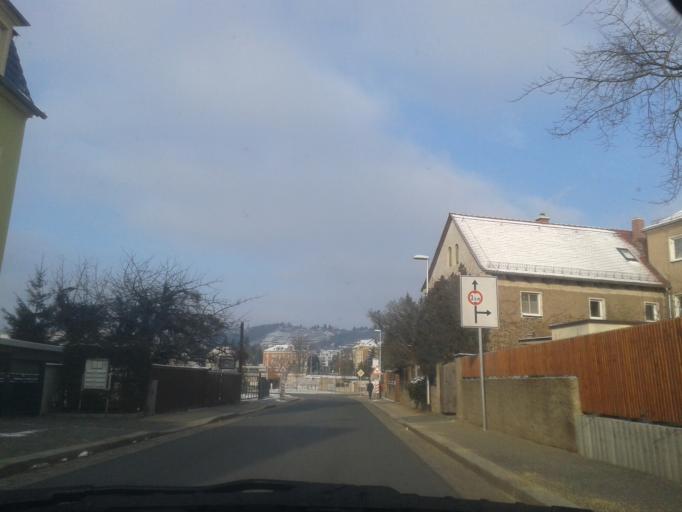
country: DE
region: Saxony
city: Radebeul
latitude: 51.0980
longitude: 13.6753
